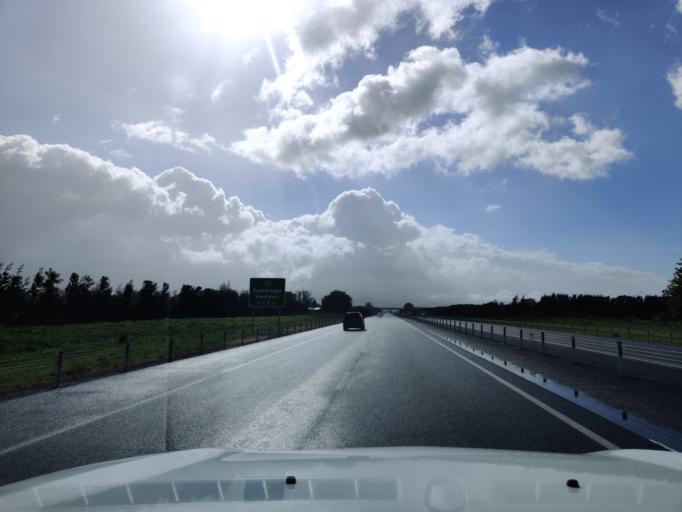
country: NZ
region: Waikato
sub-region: Waipa District
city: Cambridge
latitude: -37.8685
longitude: 175.4296
